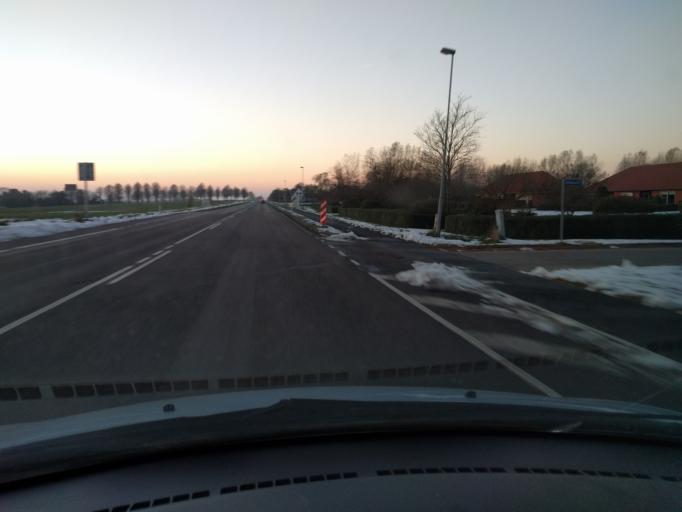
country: DK
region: South Denmark
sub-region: Nyborg Kommune
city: Ullerslev
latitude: 55.3549
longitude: 10.7225
